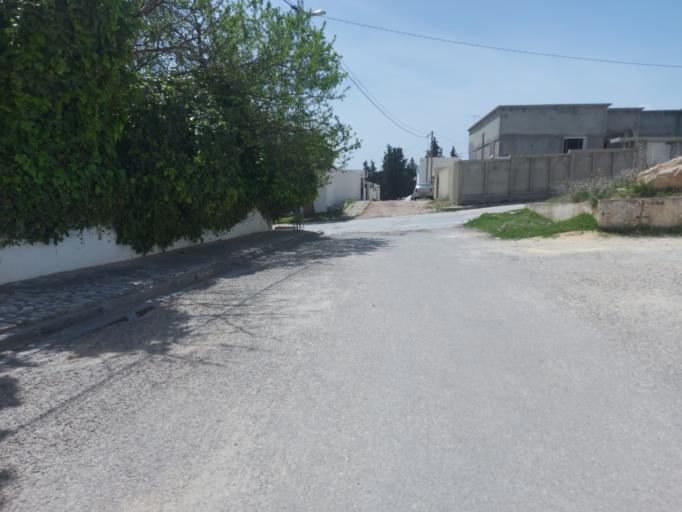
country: TN
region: Kef
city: El Kef
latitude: 36.1815
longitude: 8.7275
